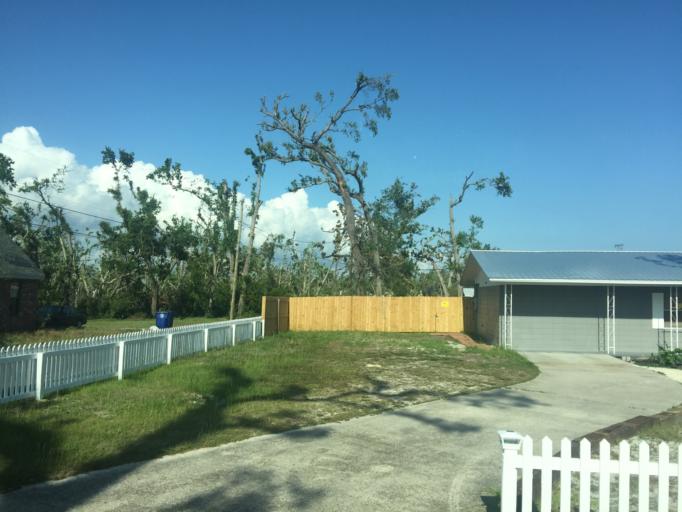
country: US
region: Florida
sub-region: Bay County
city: Springfield
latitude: 30.1516
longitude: -85.6297
